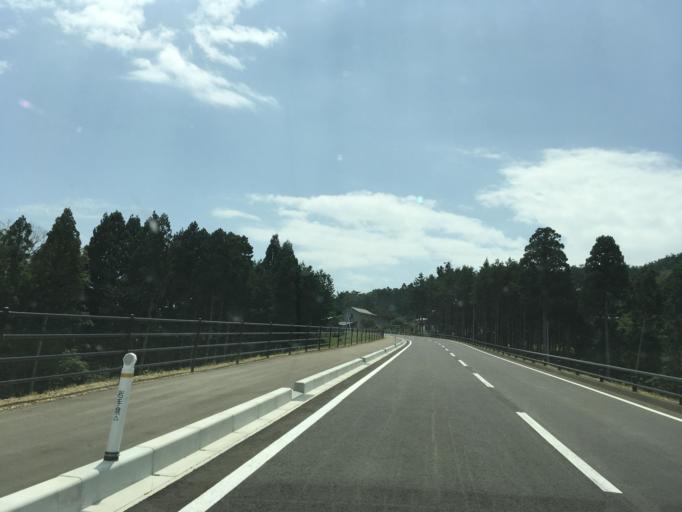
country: JP
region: Iwate
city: Ofunato
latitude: 39.0148
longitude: 141.7107
